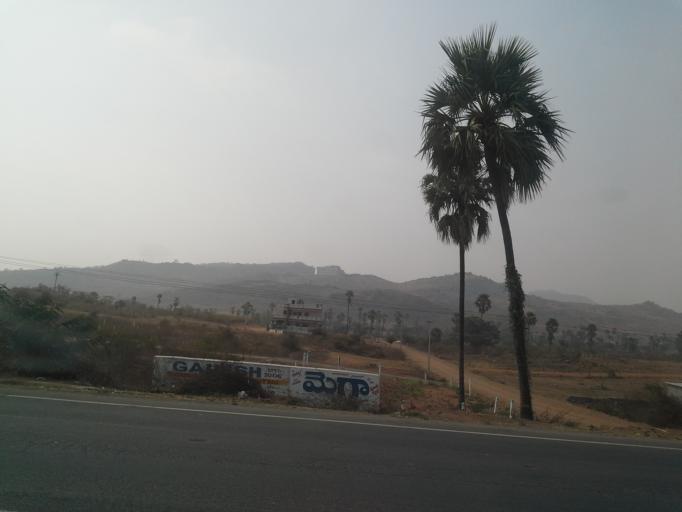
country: IN
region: Telangana
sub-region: Rangareddi
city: Lal Bahadur Nagar
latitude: 17.3143
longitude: 78.6759
